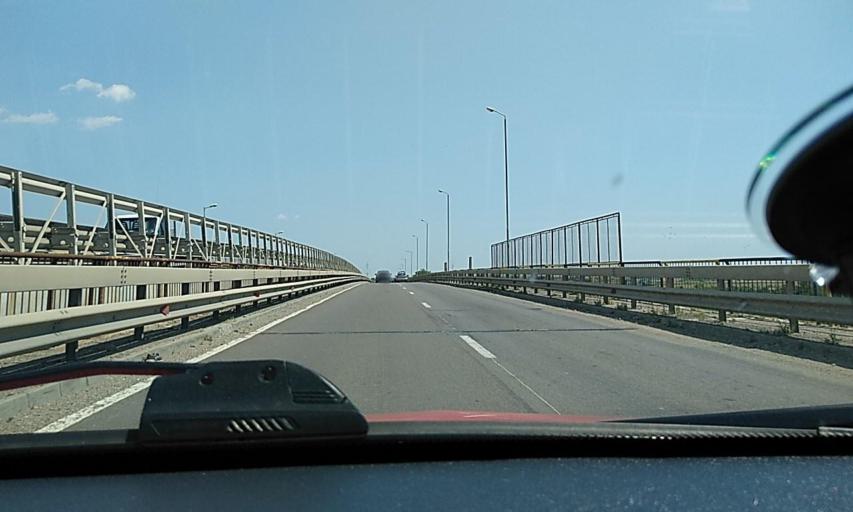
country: RO
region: Prahova
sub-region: Comuna Barcanesti
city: Tatarani
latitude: 44.8940
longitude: 26.0215
